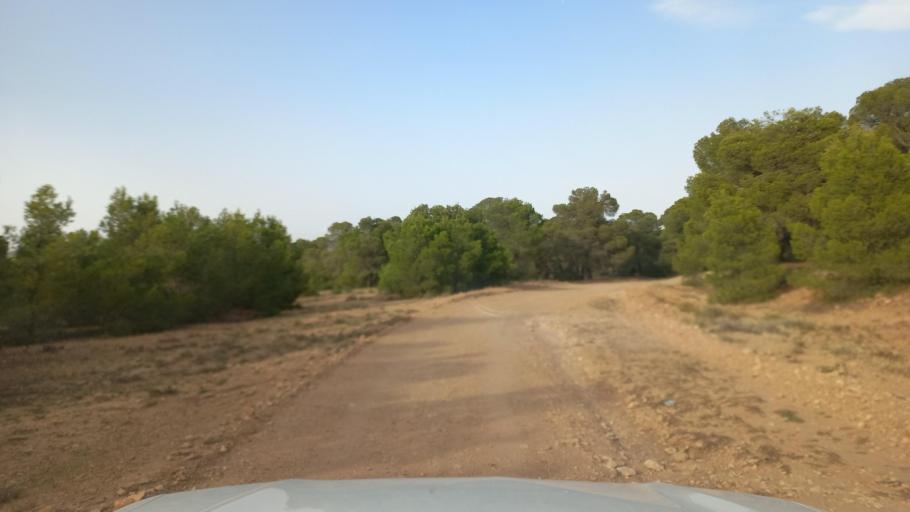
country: TN
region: Al Qasrayn
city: Kasserine
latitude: 35.3384
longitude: 8.8560
